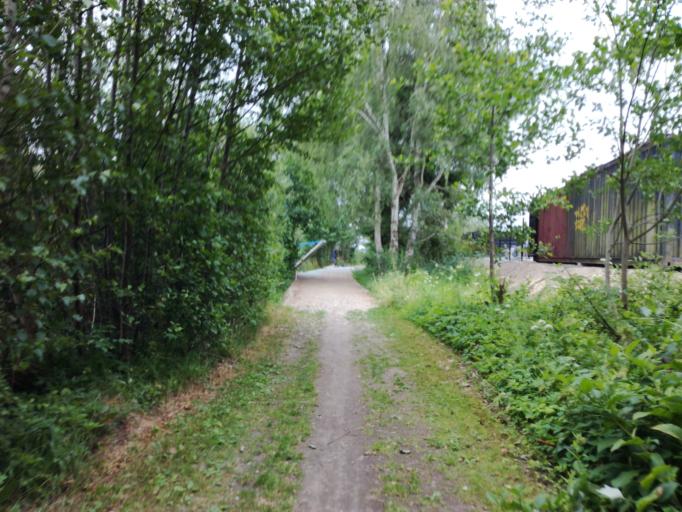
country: DK
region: South Denmark
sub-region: Vejle Kommune
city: Vejle
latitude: 55.7018
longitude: 9.5523
